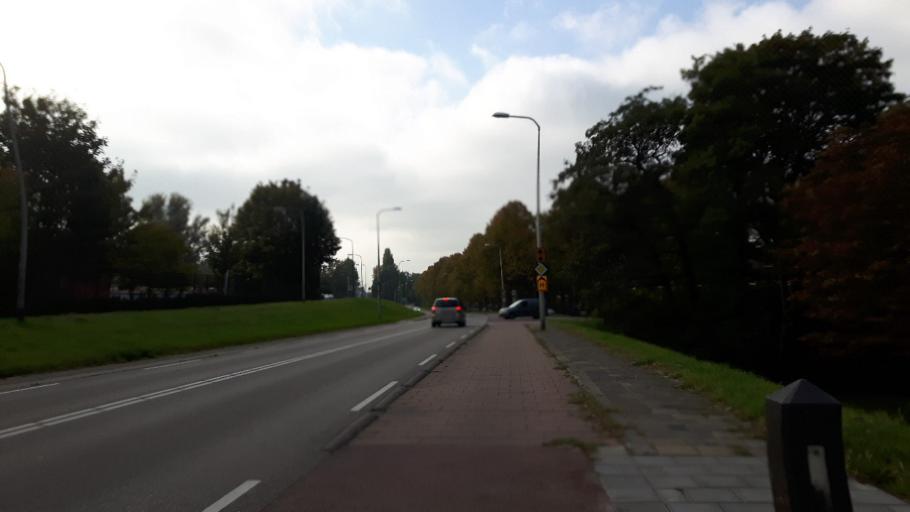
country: NL
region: South Holland
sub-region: Gemeente Gouda
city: Gouda
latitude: 52.0040
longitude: 4.7075
